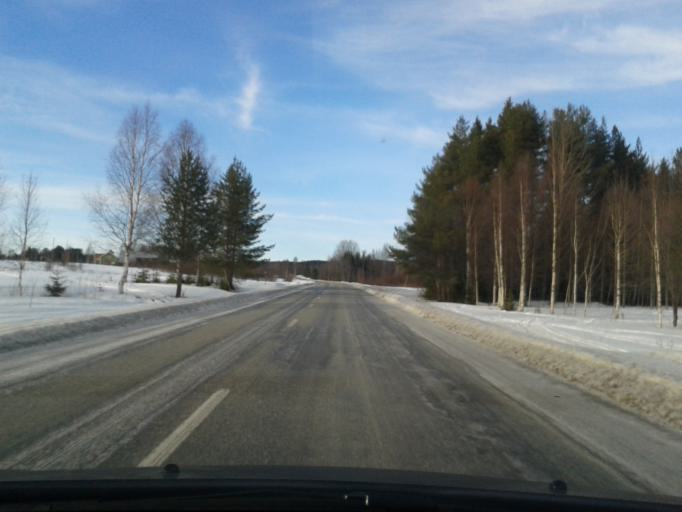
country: SE
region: Vaesternorrland
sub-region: OErnskoeldsviks Kommun
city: Bredbyn
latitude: 63.5681
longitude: 17.9311
